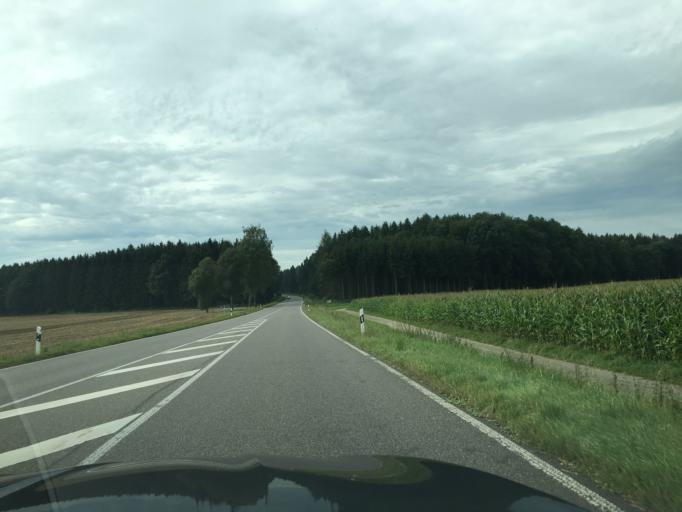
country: DE
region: Baden-Wuerttemberg
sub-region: Tuebingen Region
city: Emeringen
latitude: 48.2039
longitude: 9.5319
